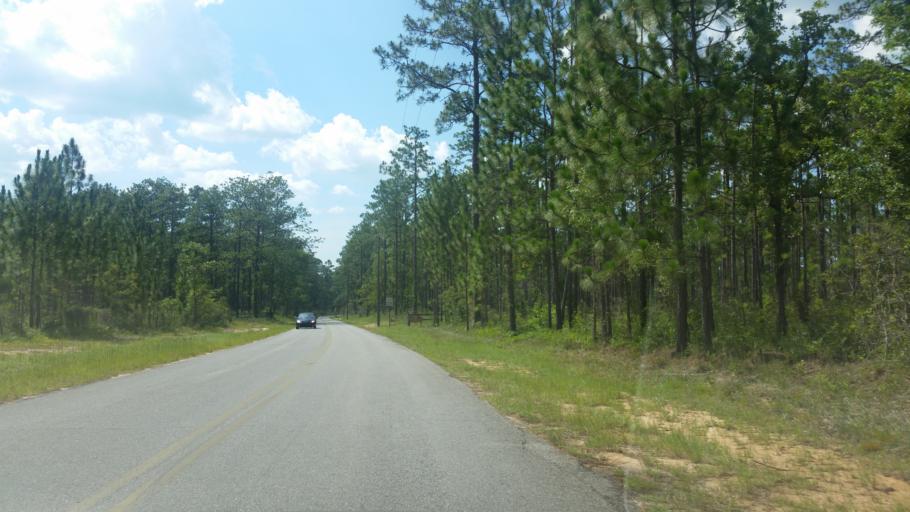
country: US
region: Florida
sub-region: Santa Rosa County
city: East Milton
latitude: 30.6996
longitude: -86.8763
